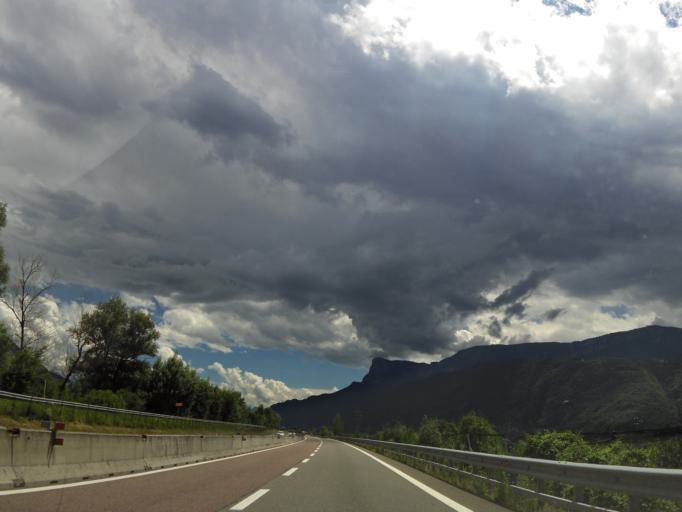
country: IT
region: Trentino-Alto Adige
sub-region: Bolzano
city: Gargazzone
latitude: 46.5871
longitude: 11.1872
